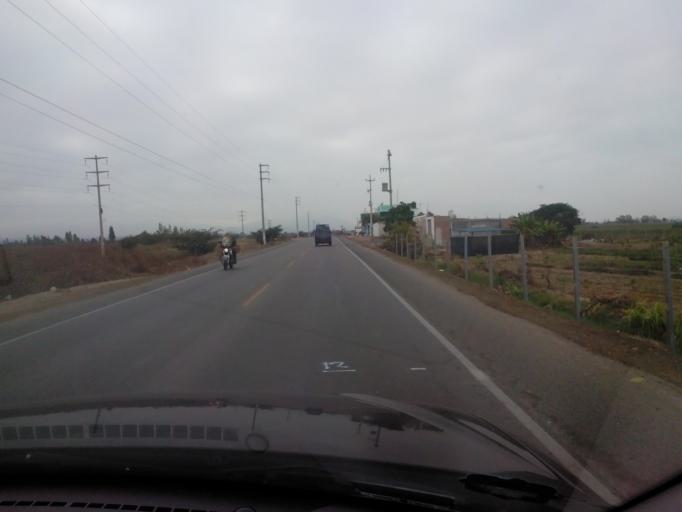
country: PE
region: Ica
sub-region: Provincia de Pisco
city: Independencia
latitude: -13.6843
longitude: -76.0508
